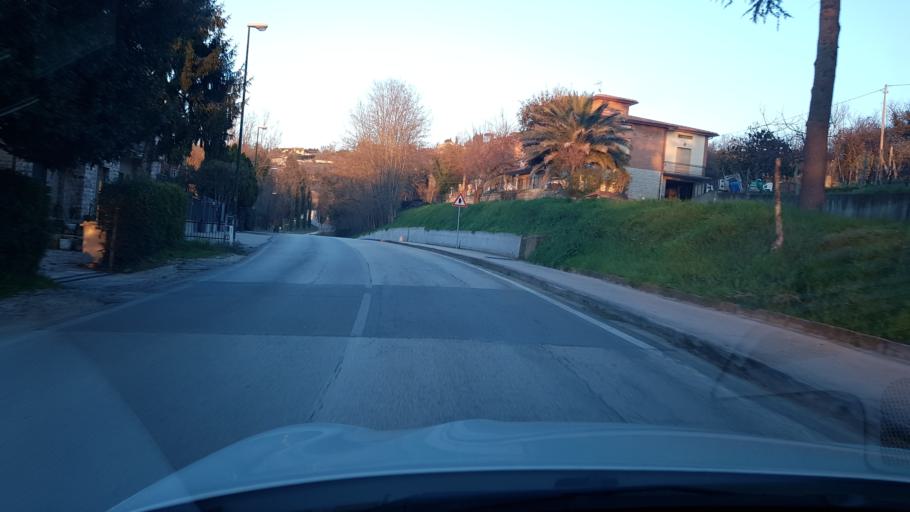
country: IT
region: Umbria
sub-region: Provincia di Perugia
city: Torgiano
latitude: 43.0110
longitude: 12.4334
